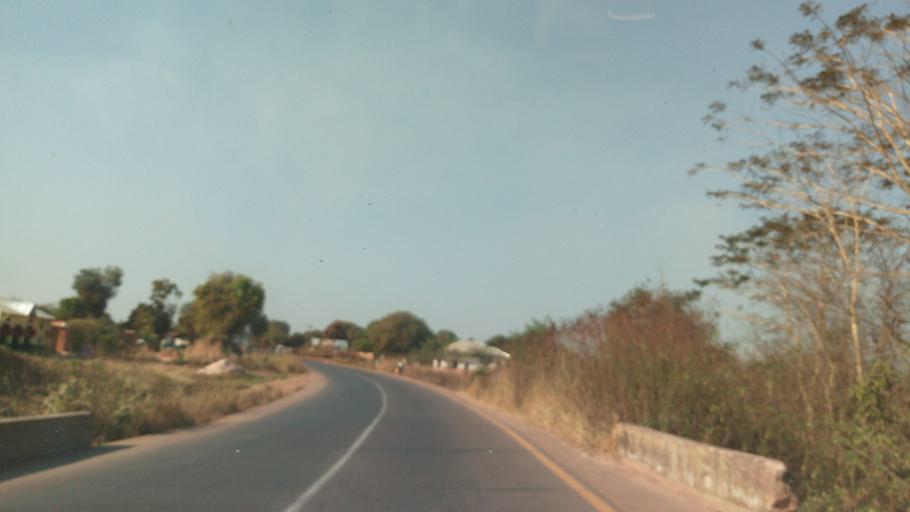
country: CD
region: Katanga
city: Lubumbashi
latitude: -11.4517
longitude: 27.7082
